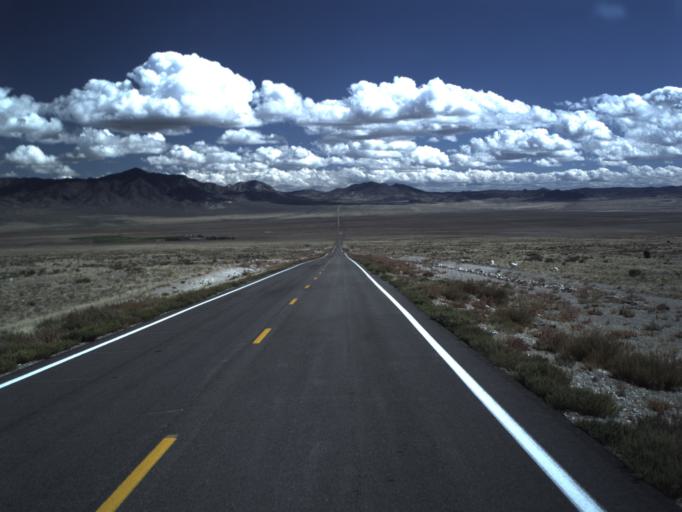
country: US
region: Utah
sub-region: Beaver County
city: Milford
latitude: 38.4981
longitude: -113.4919
